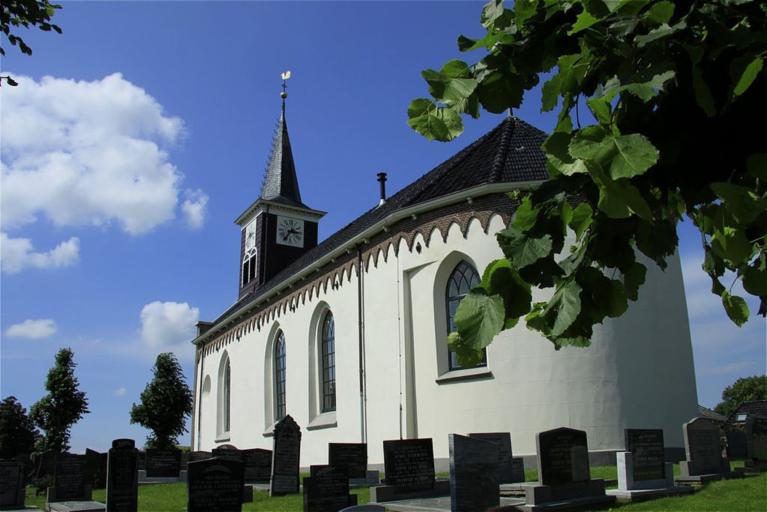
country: NL
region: Friesland
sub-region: Gemeente Franekeradeel
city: Tzum
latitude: 53.1259
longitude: 5.5307
